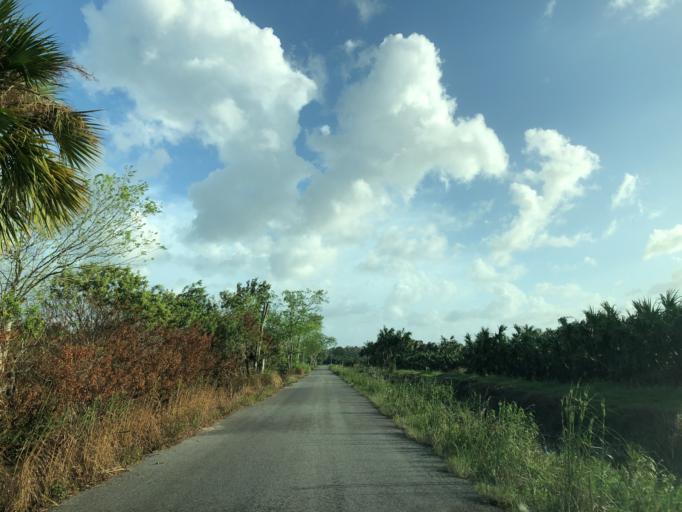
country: US
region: Florida
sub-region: Seminole County
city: Oviedo
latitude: 28.6985
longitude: -81.1799
